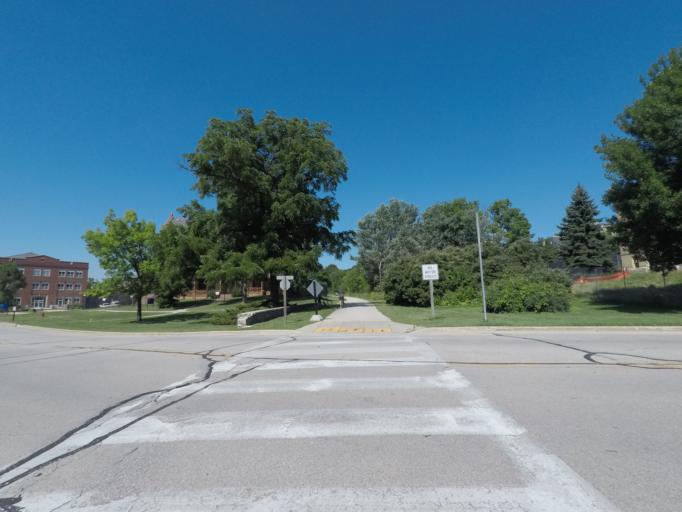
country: US
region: Wisconsin
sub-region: Milwaukee County
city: West Milwaukee
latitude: 43.0255
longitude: -87.9756
